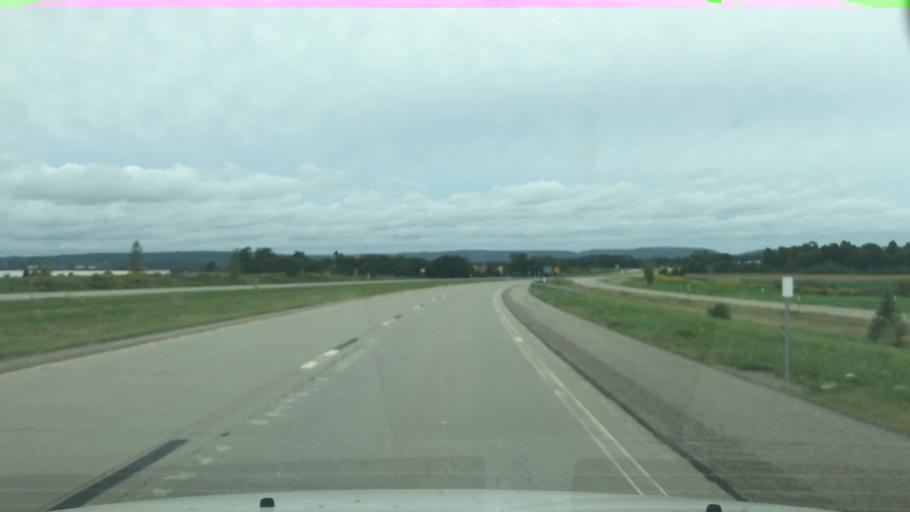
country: US
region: New York
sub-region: Erie County
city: Springville
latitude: 42.5070
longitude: -78.6924
